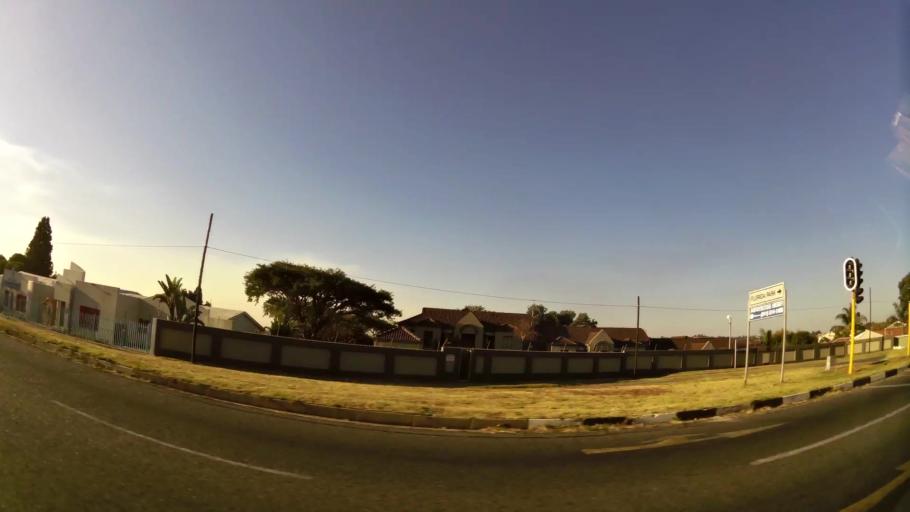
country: ZA
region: Gauteng
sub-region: City of Johannesburg Metropolitan Municipality
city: Roodepoort
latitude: -26.1625
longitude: 27.9224
